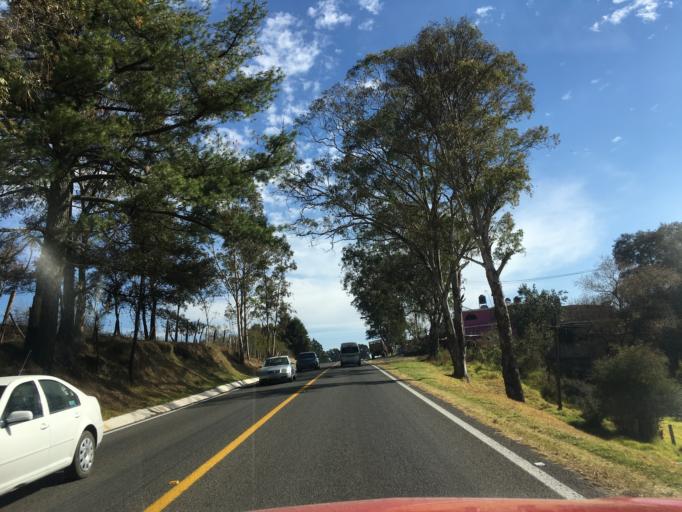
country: MX
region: Michoacan
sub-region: Hidalgo
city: San Lucas Huarirapeo (La Mesa de San Lucas)
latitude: 19.6659
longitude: -100.6785
